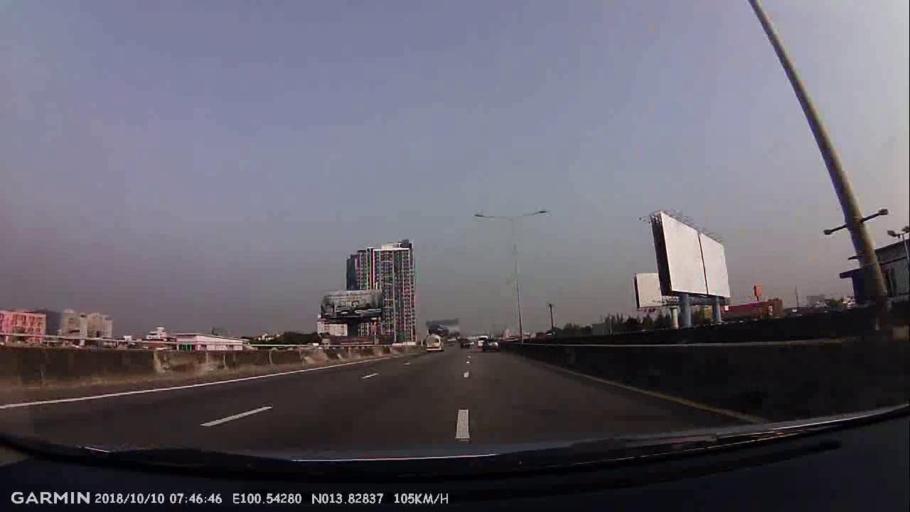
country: TH
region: Bangkok
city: Chatuchak
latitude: 13.8286
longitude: 100.5426
